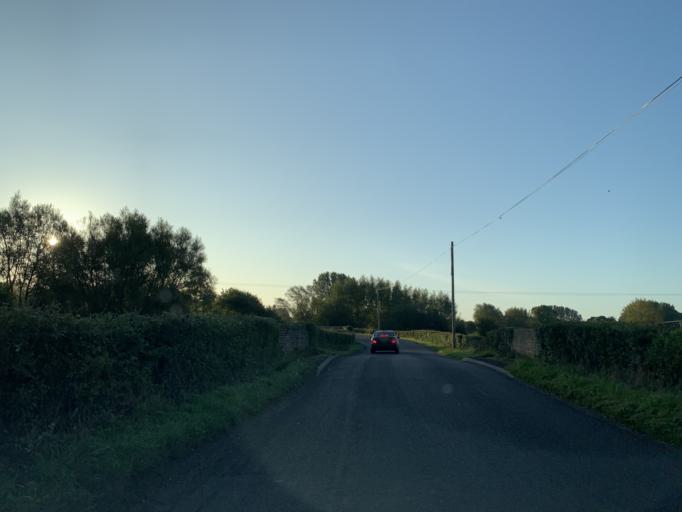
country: GB
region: England
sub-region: Wiltshire
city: Woodford
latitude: 51.0966
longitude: -1.8196
